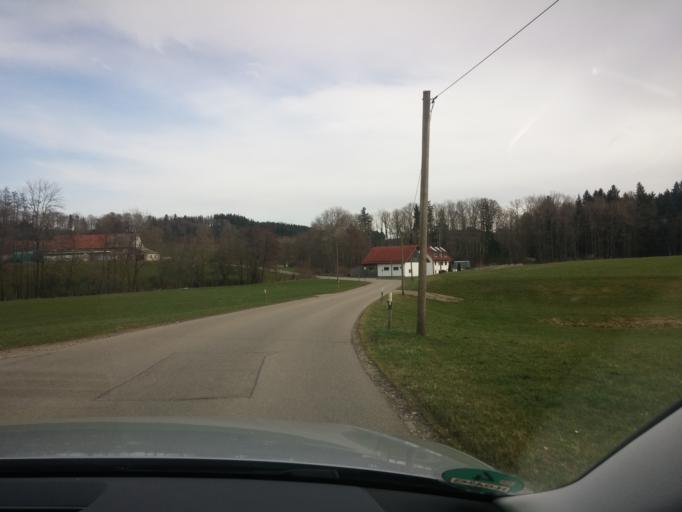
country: DE
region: Bavaria
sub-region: Swabia
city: Kronburg
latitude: 47.9085
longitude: 10.1735
